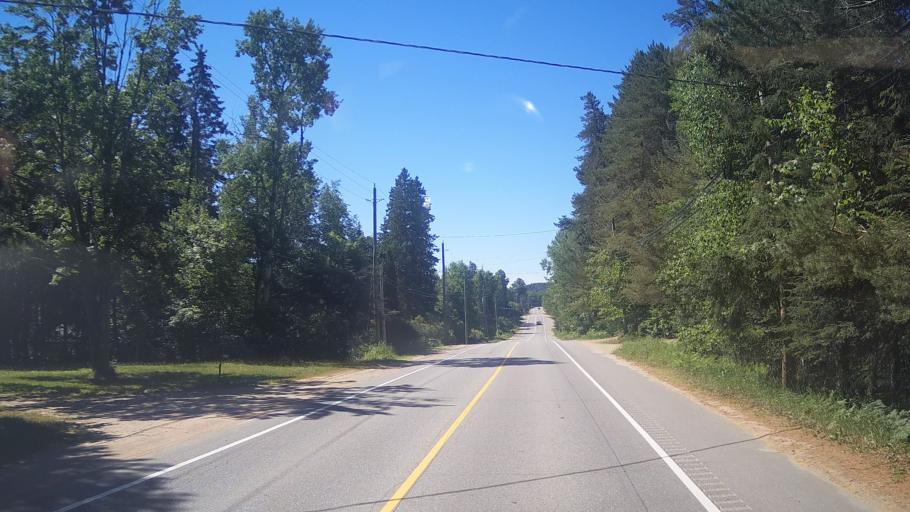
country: CA
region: Ontario
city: Huntsville
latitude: 45.3494
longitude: -79.2014
